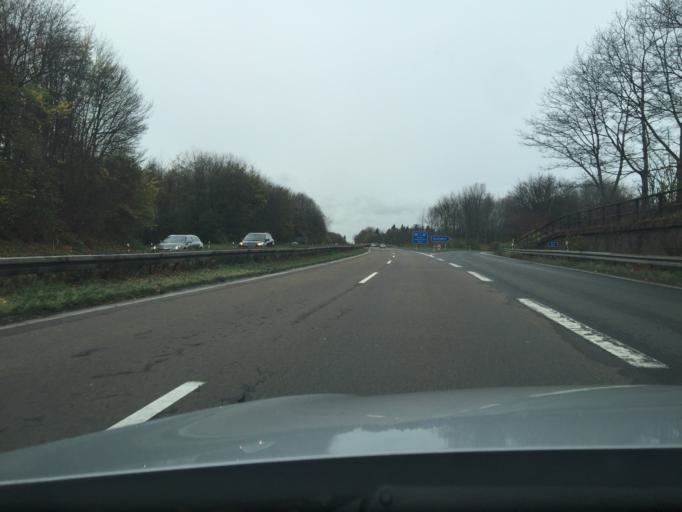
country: DE
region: North Rhine-Westphalia
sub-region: Regierungsbezirk Dusseldorf
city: Velbert
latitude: 51.3388
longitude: 7.0602
